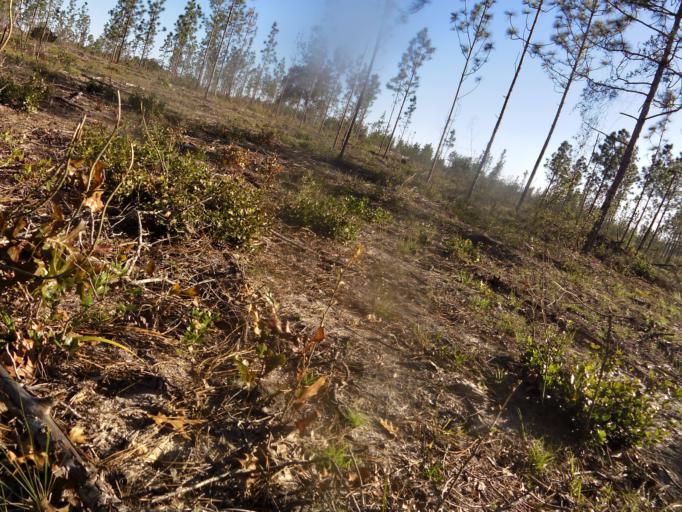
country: US
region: Florida
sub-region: Clay County
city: Keystone Heights
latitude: 29.8375
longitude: -81.9808
